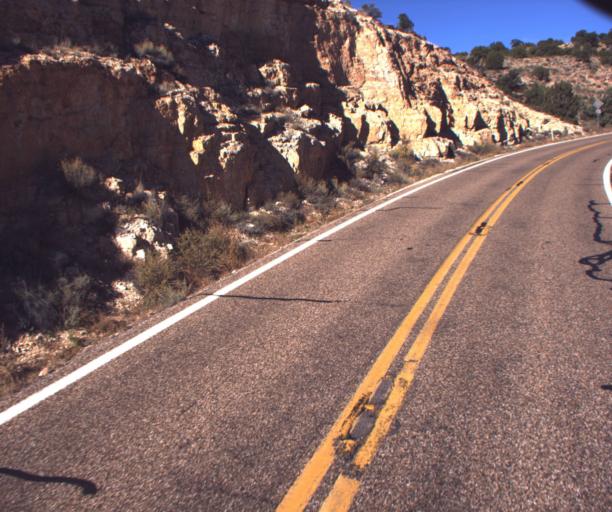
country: US
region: Arizona
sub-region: Coconino County
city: Fredonia
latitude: 36.7233
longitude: -112.0640
